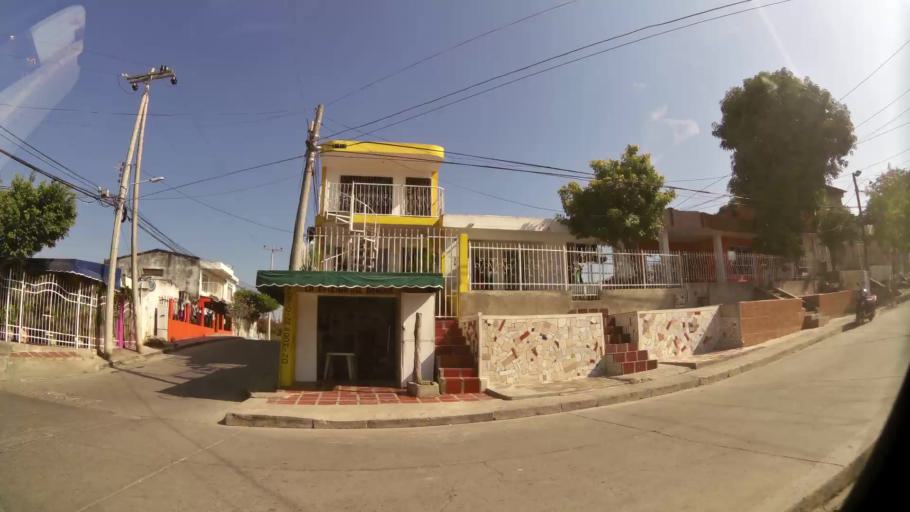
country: CO
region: Bolivar
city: Cartagena
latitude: 10.3981
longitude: -75.5010
